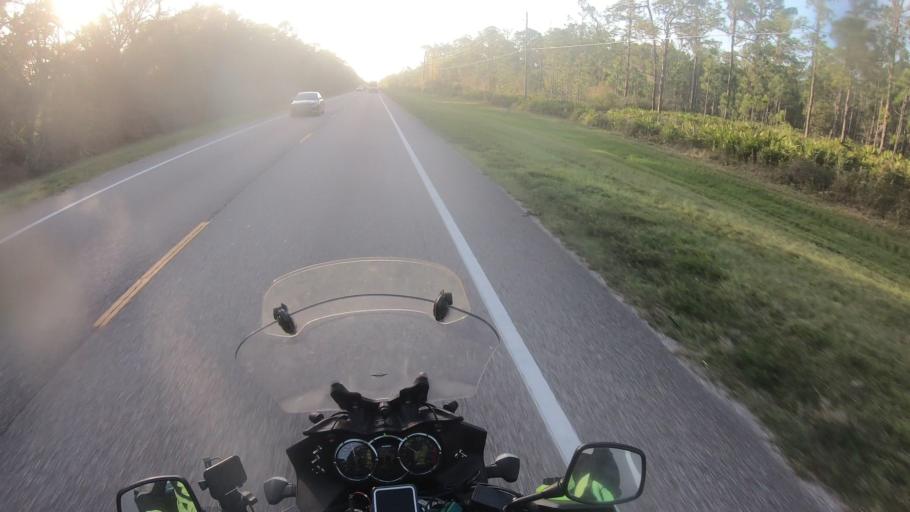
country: US
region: Florida
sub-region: Sarasota County
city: The Meadows
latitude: 27.4085
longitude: -82.3318
